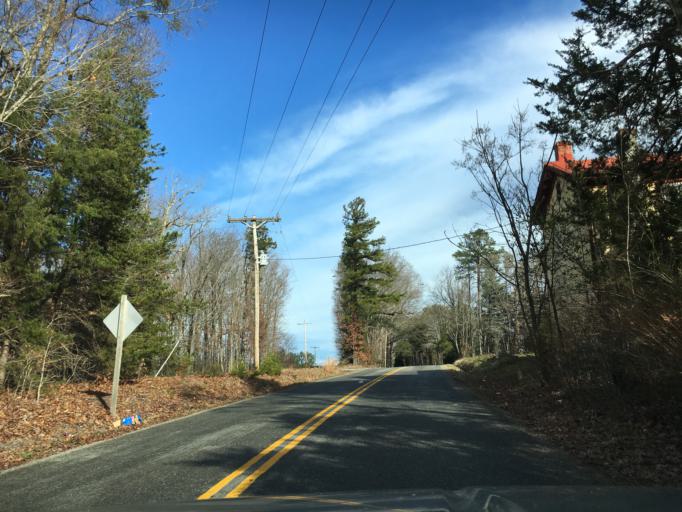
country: US
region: Virginia
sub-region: Nottoway County
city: Crewe
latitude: 37.2810
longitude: -78.2045
